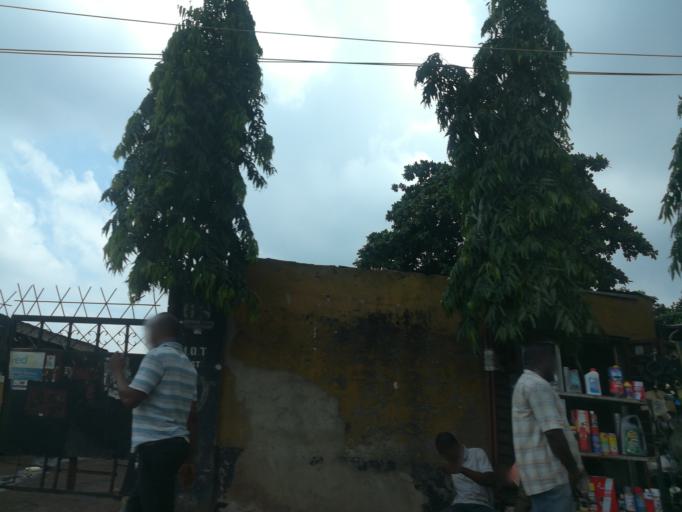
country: NG
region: Lagos
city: Ojota
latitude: 6.5987
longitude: 3.3665
